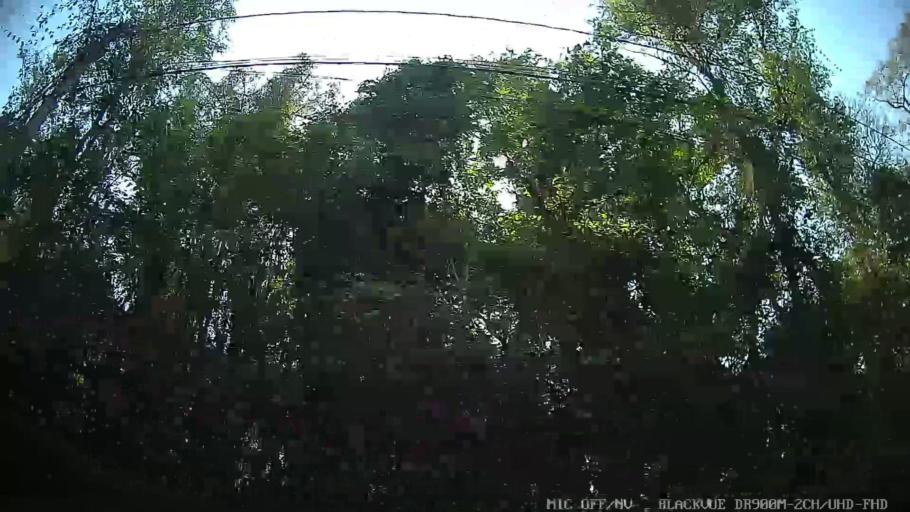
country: BR
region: Sao Paulo
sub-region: Itatiba
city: Itatiba
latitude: -23.0167
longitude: -46.8543
